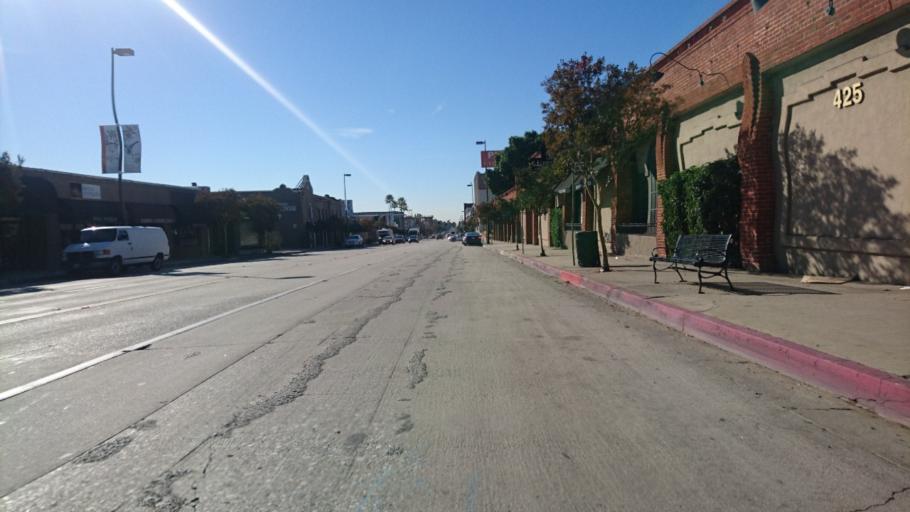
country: US
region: California
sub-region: Los Angeles County
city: Pasadena
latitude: 34.1383
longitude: -118.1505
